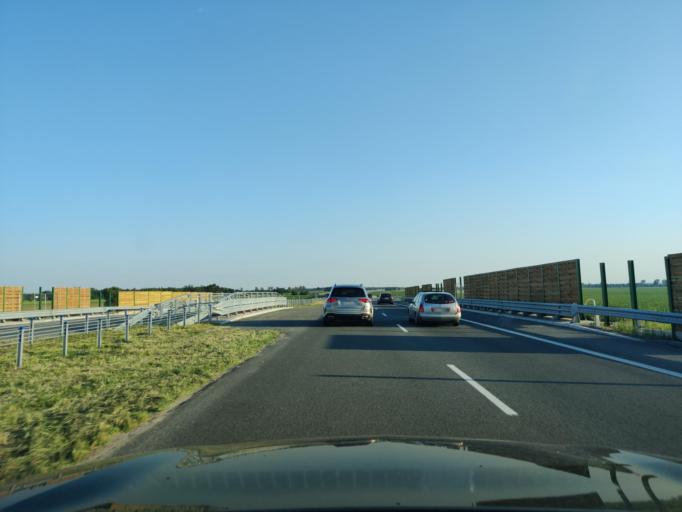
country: PL
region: Masovian Voivodeship
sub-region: Powiat mlawski
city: Wisniewo
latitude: 53.0494
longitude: 20.3608
